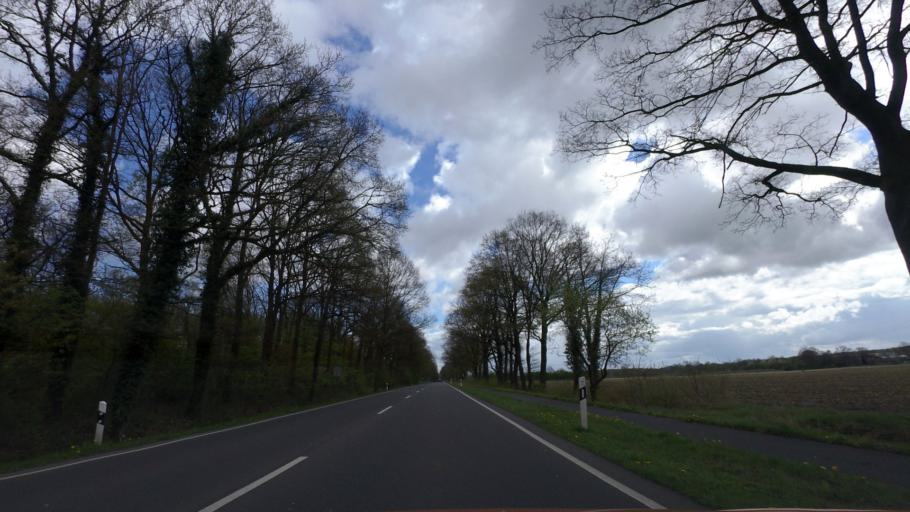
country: DE
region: Lower Saxony
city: Hassendorf
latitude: 53.1190
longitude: 9.2786
